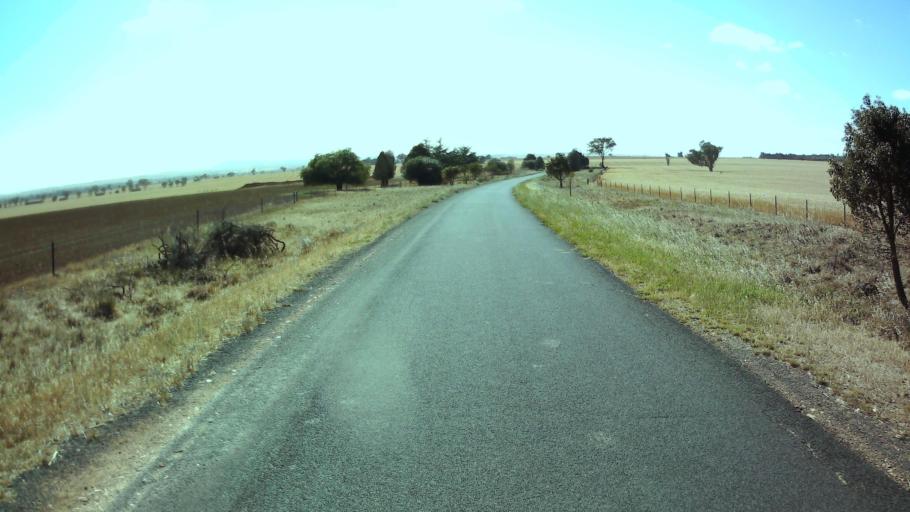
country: AU
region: New South Wales
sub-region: Weddin
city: Grenfell
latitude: -34.0597
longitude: 148.2465
